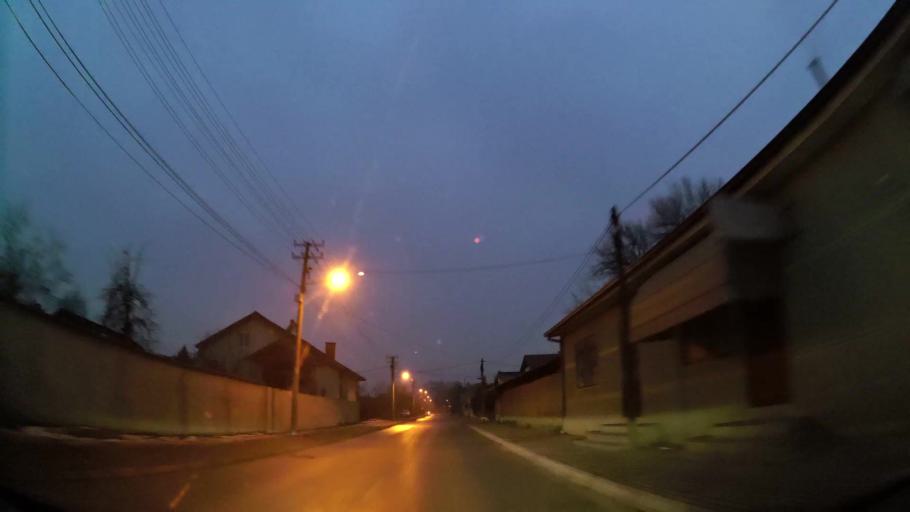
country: MK
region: Kisela Voda
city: Kisela Voda
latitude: 41.9679
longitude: 21.4890
